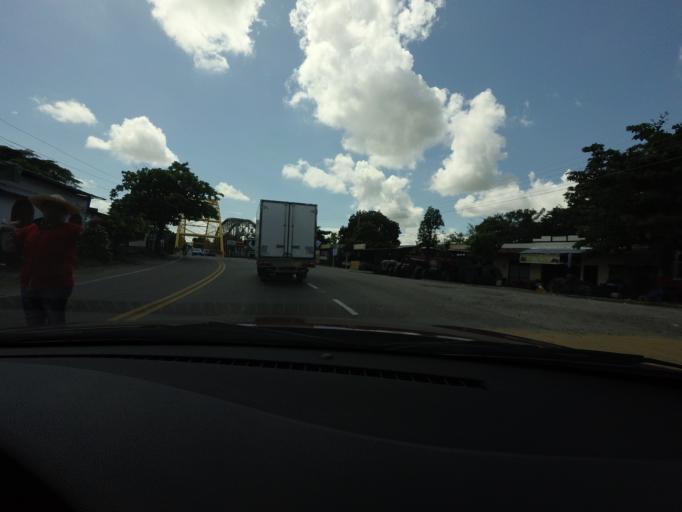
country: CO
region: Tolima
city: Saldana
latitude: 3.9358
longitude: -75.0192
